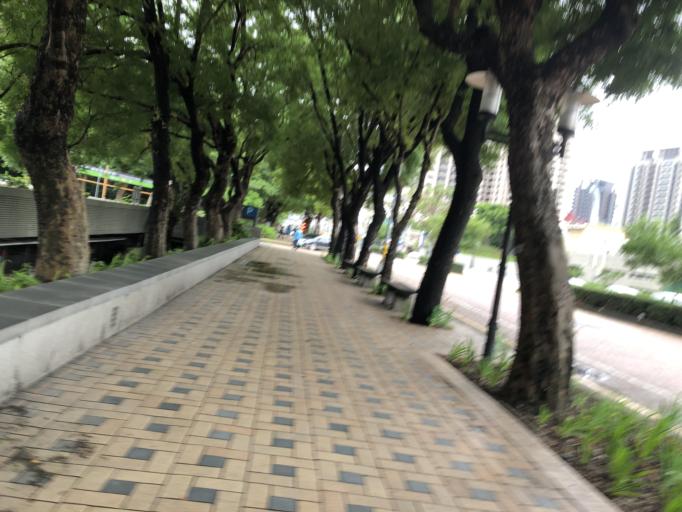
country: TW
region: Taiwan
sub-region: Taichung City
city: Taichung
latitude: 24.1576
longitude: 120.6676
